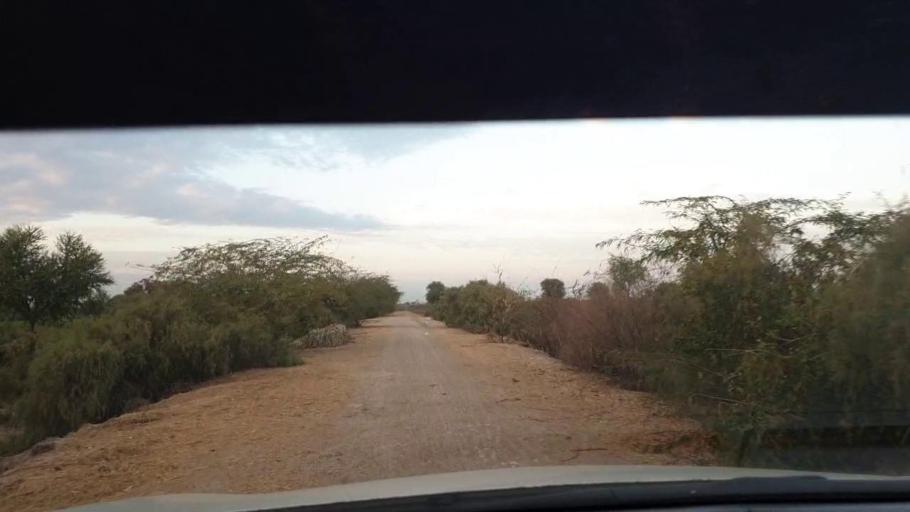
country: PK
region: Sindh
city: Berani
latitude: 25.8022
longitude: 68.8088
